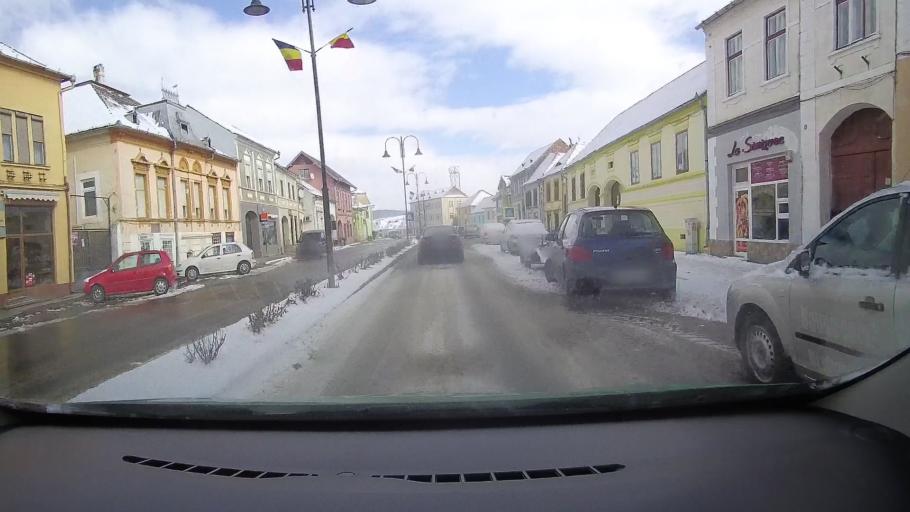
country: RO
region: Sibiu
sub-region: Oras Agnita
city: Agnita
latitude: 45.9755
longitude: 24.6236
